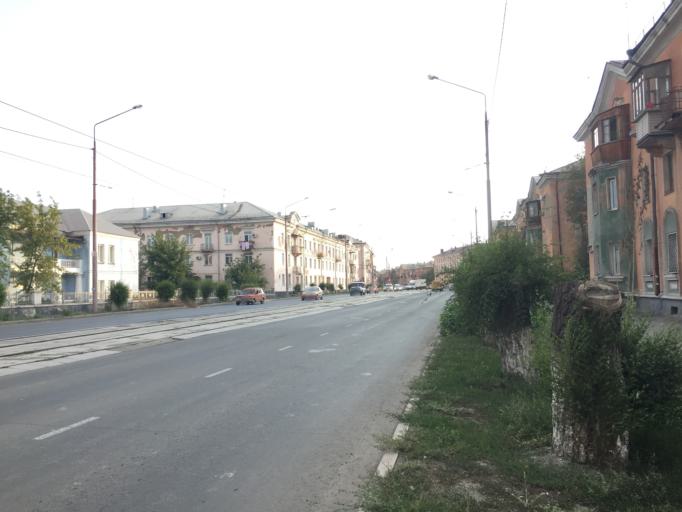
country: RU
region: Orenburg
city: Novotroitsk
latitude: 51.2001
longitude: 58.3366
